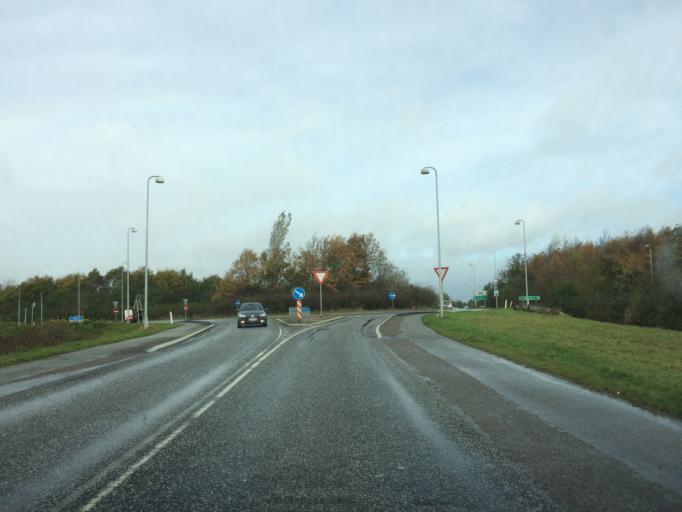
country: DK
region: South Denmark
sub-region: Fredericia Kommune
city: Taulov
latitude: 55.5370
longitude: 9.6380
